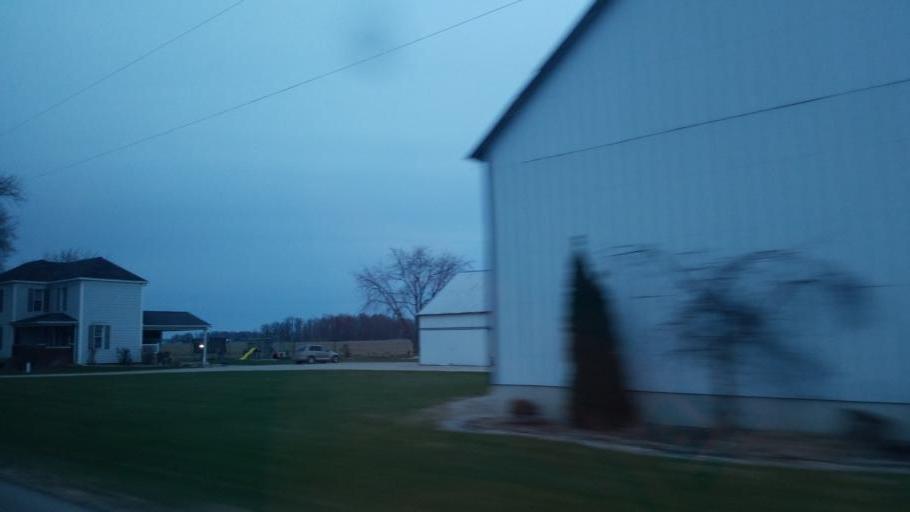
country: US
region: Indiana
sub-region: Adams County
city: Berne
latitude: 40.7214
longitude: -84.8983
